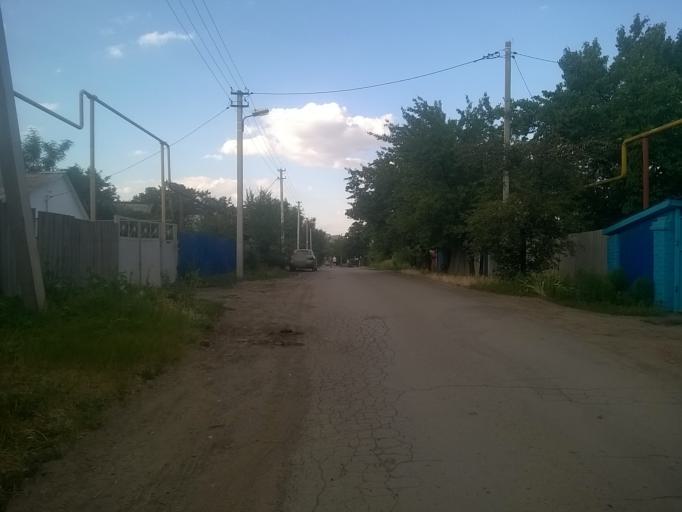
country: RU
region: Rostov
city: Donetsk
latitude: 48.3412
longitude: 39.9608
